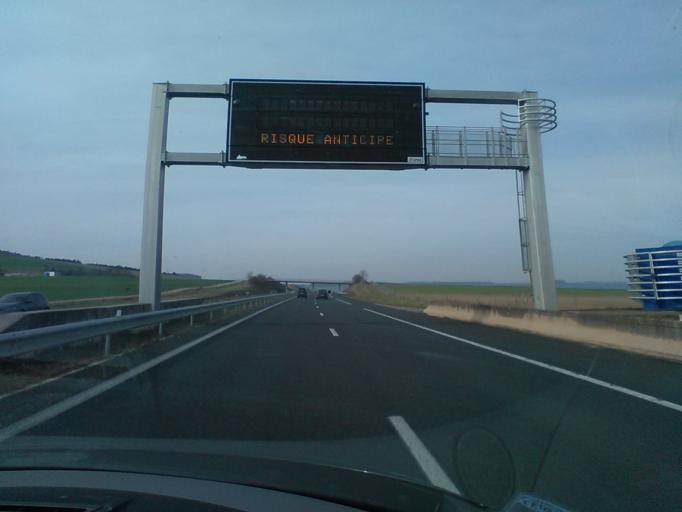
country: FR
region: Champagne-Ardenne
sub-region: Departement de l'Aube
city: Saint-Germain
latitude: 48.2526
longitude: 3.9820
